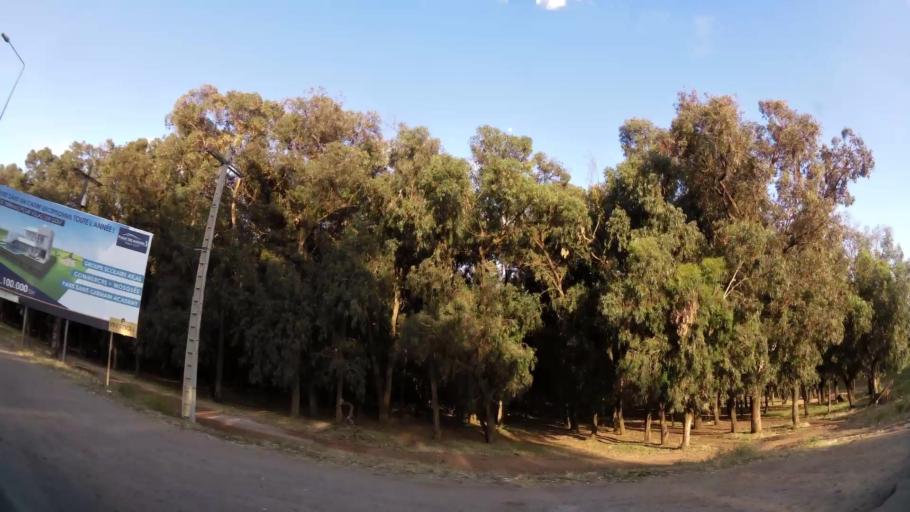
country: MA
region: Rabat-Sale-Zemmour-Zaer
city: Sale
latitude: 34.1307
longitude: -6.7328
